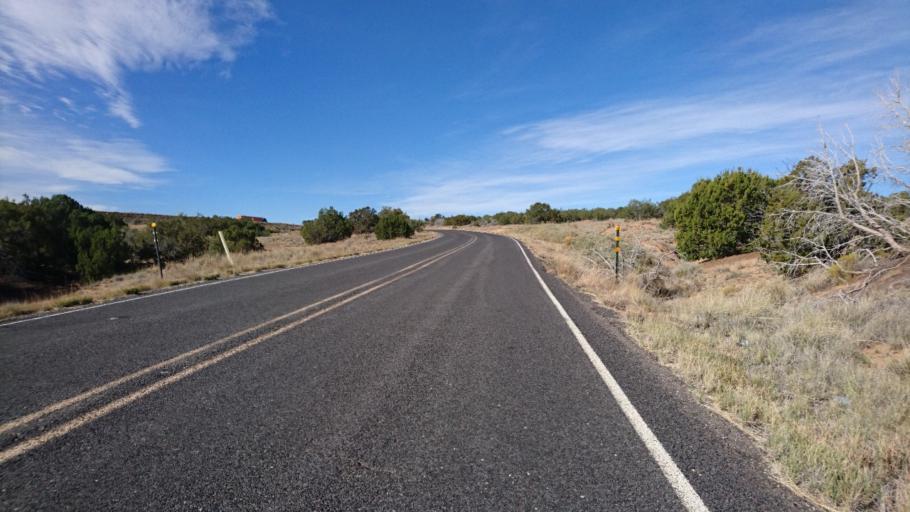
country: US
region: New Mexico
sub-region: Cibola County
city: Laguna
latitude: 35.0407
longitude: -107.3603
